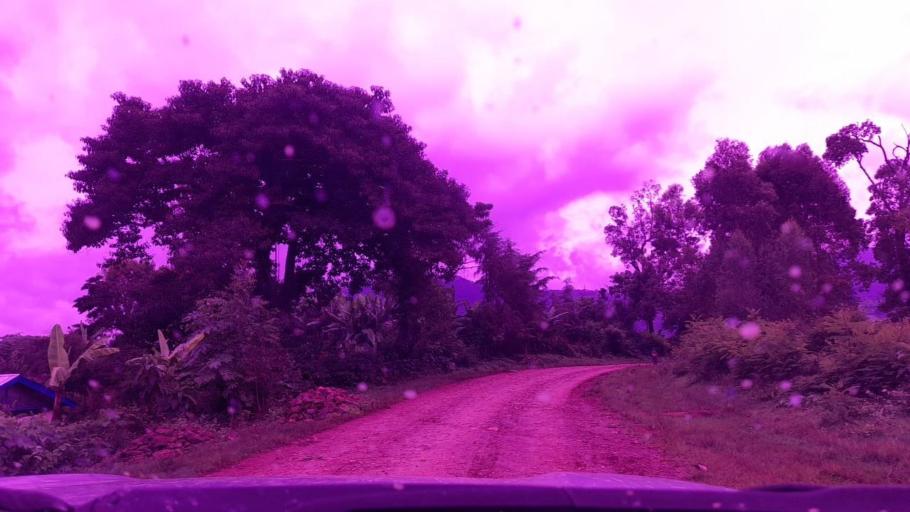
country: ET
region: Southern Nations, Nationalities, and People's Region
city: Bonga
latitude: 7.5503
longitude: 35.8399
